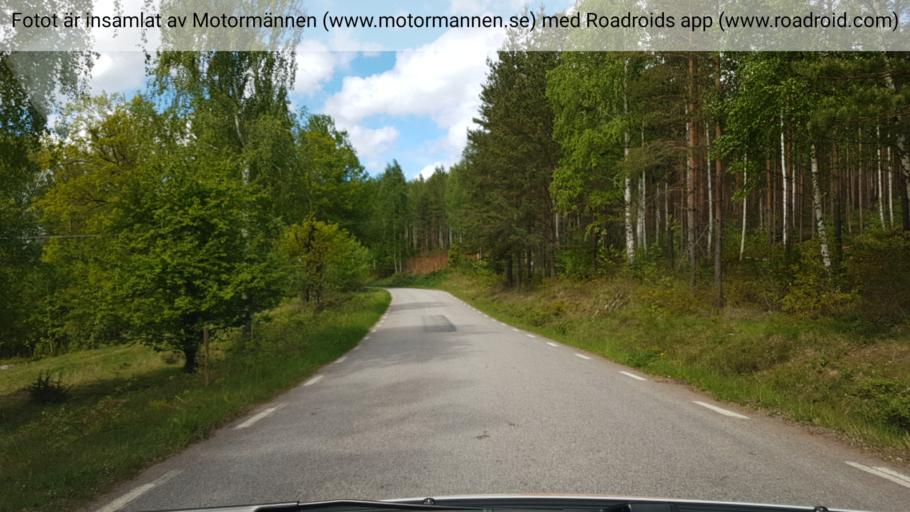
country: SE
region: Kalmar
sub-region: Vasterviks Kommun
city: Forserum
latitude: 57.8452
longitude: 16.5364
